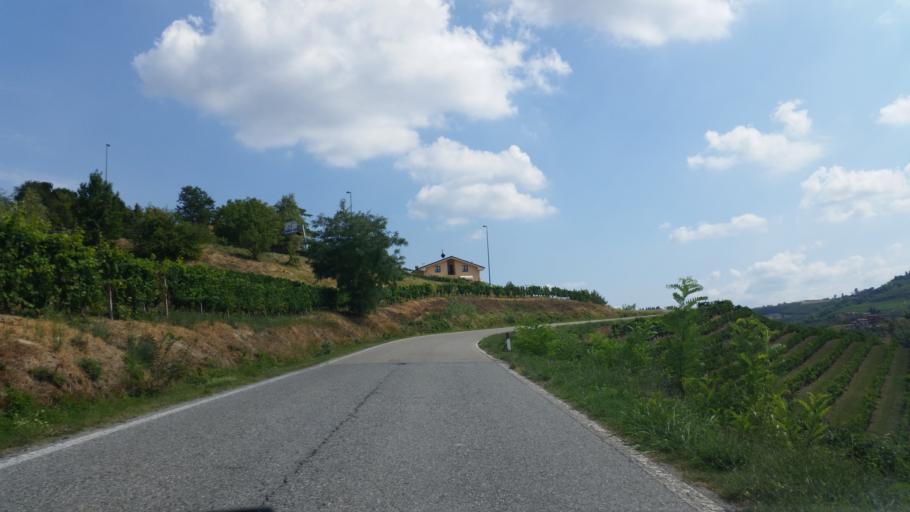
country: IT
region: Piedmont
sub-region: Provincia di Cuneo
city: Mango
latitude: 44.6897
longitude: 8.1453
